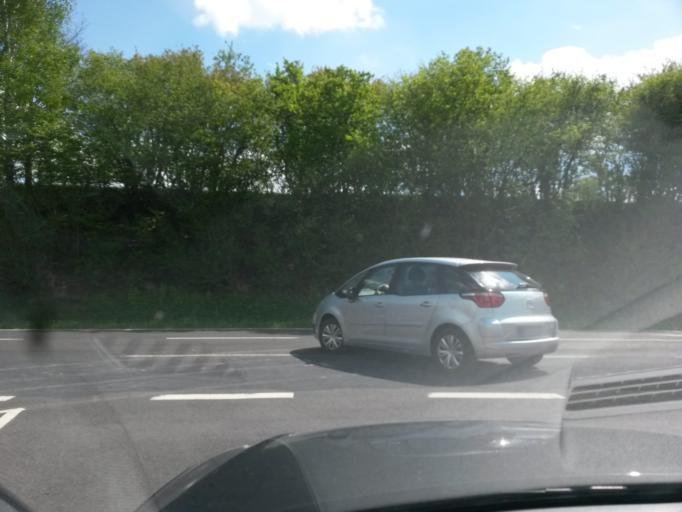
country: DE
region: Hesse
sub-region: Regierungsbezirk Kassel
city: Poppenhausen
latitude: 50.4972
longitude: 9.8912
